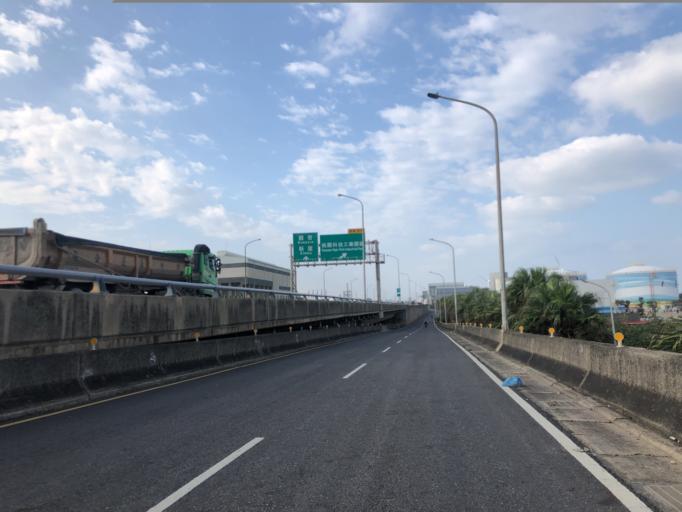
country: TW
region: Taiwan
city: Taoyuan City
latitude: 25.0567
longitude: 121.0988
